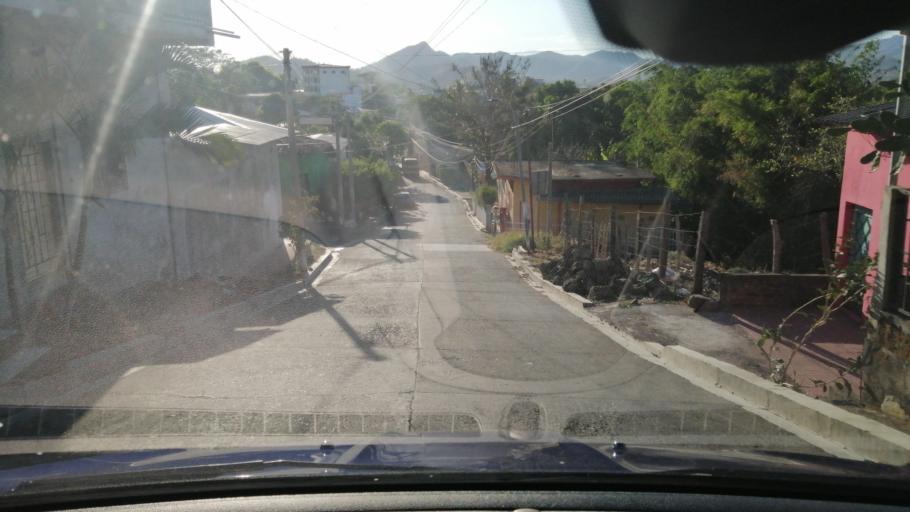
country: SV
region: Santa Ana
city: Metapan
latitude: 14.3318
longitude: -89.4391
